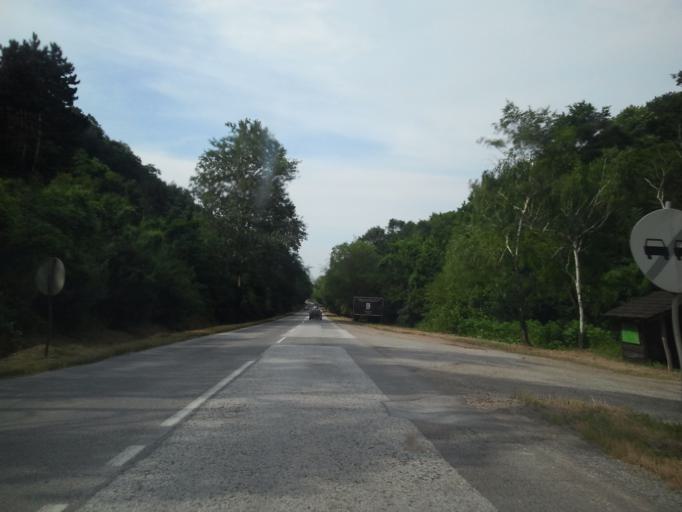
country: RS
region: Autonomna Pokrajina Vojvodina
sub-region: Juznobacki Okrug
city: Novi Sad
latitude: 45.1797
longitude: 19.8389
